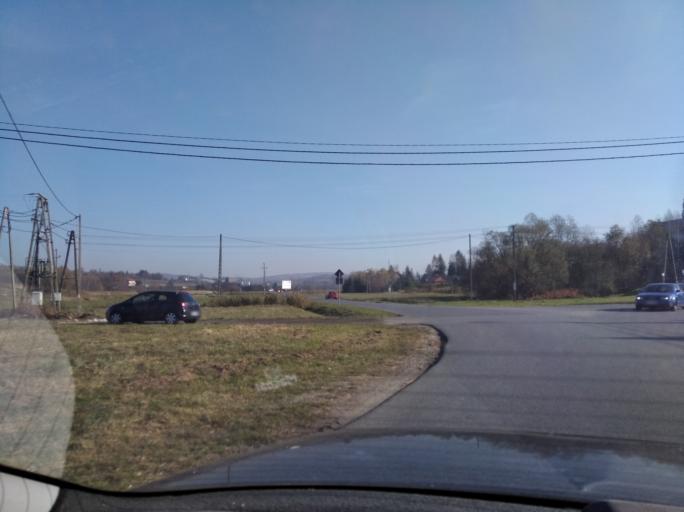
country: PL
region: Subcarpathian Voivodeship
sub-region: Powiat ropczycko-sedziszowski
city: Wielopole Skrzynskie
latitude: 49.9462
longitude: 21.6091
